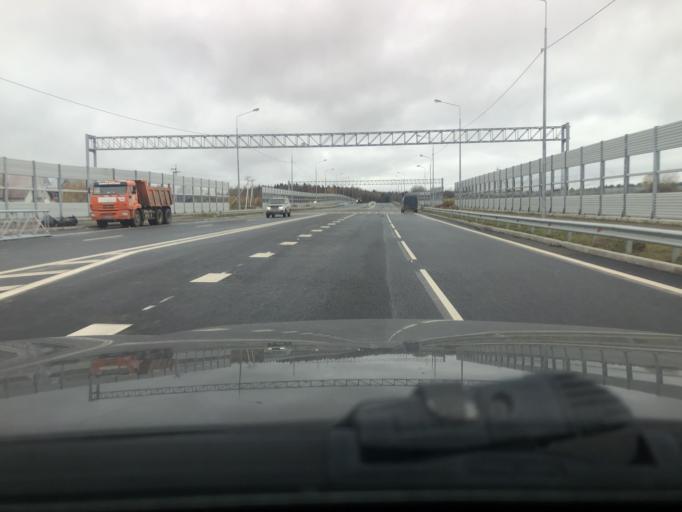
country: RU
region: Moskovskaya
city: Semkhoz
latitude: 56.3235
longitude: 38.0766
